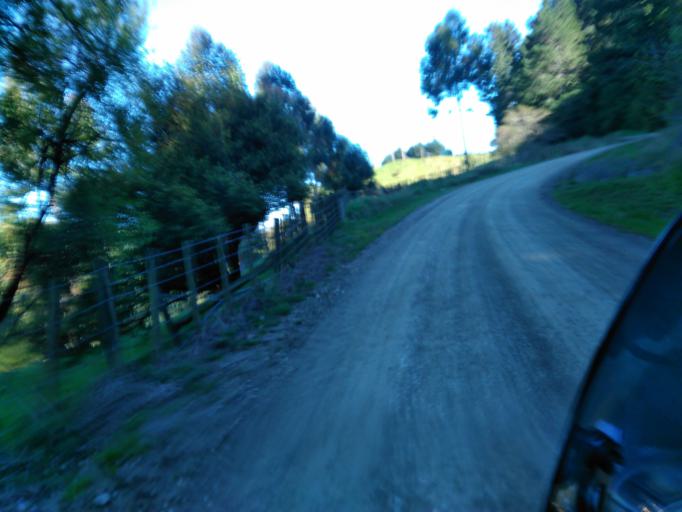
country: NZ
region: Gisborne
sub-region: Gisborne District
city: Gisborne
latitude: -38.4084
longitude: 177.6833
